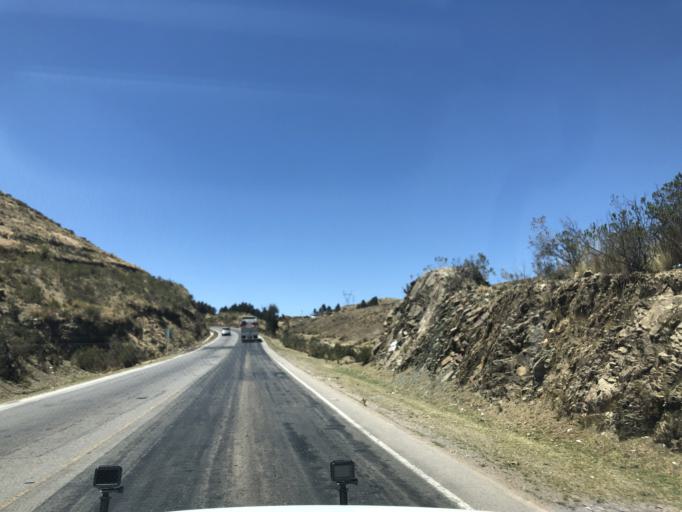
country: BO
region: Cochabamba
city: Irpa Irpa
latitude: -17.6544
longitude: -66.4666
